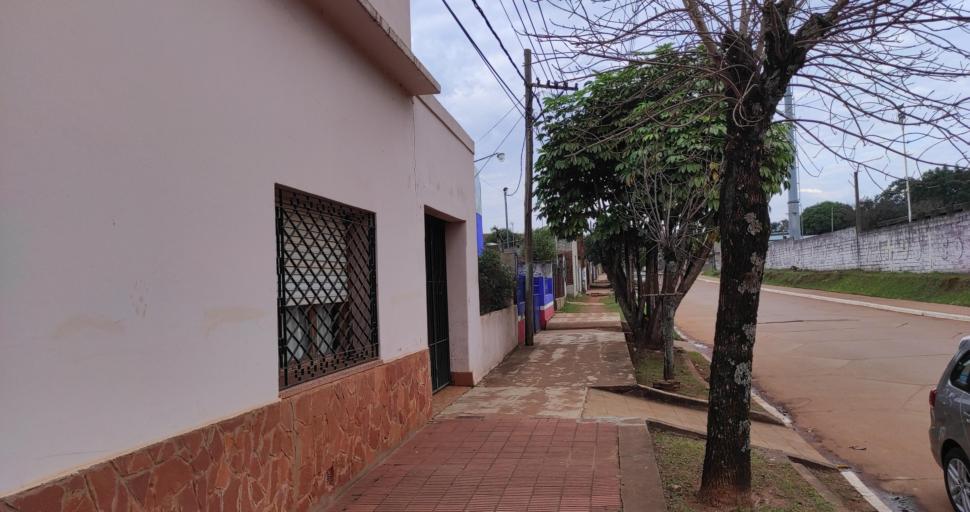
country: AR
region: Corrientes
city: Santo Tome
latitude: -28.5535
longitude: -56.0391
